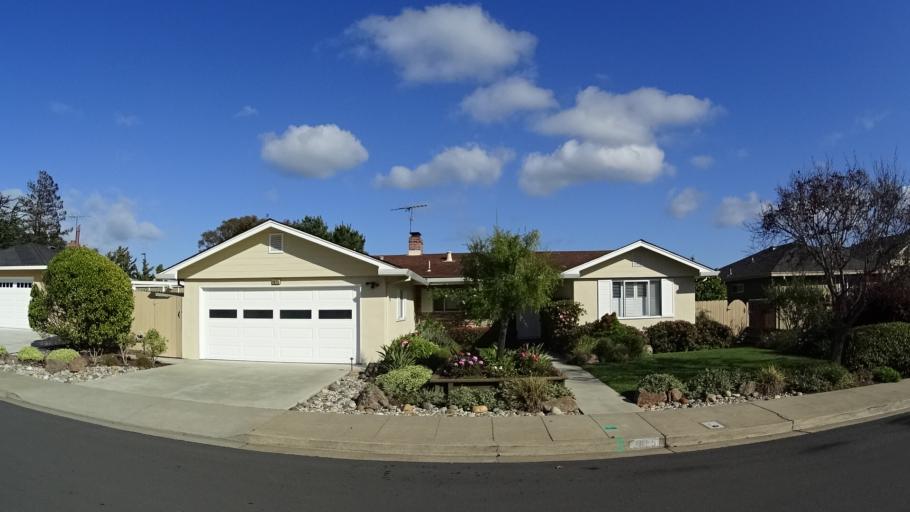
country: US
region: California
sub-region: San Mateo County
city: Millbrae
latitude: 37.5866
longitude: -122.3886
